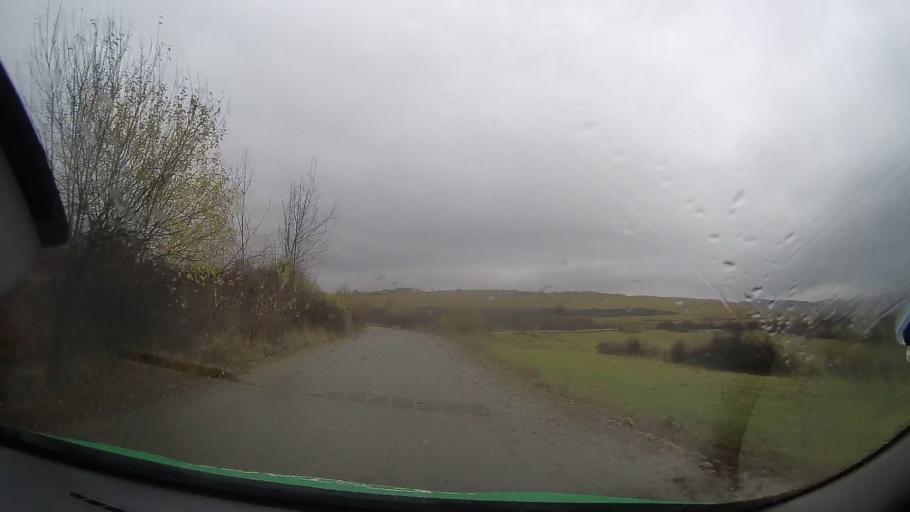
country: RO
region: Mures
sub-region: Comuna Vatava
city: Vatava
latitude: 46.9512
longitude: 24.7345
